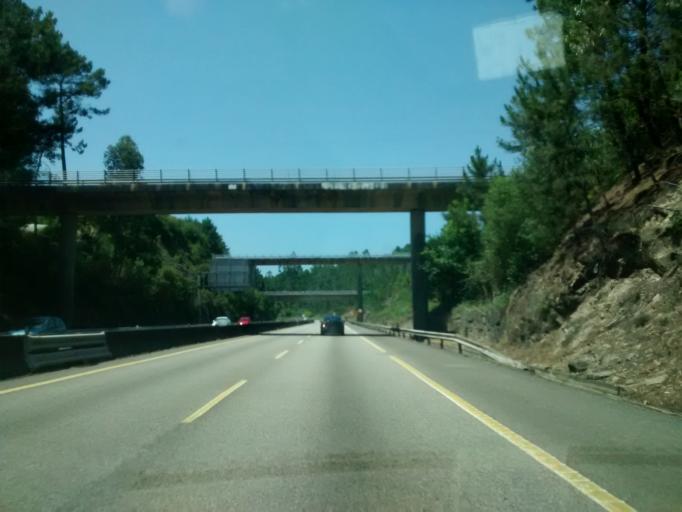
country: ES
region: Galicia
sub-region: Provincia de Pontevedra
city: Porrino
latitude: 42.1785
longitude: -8.6260
